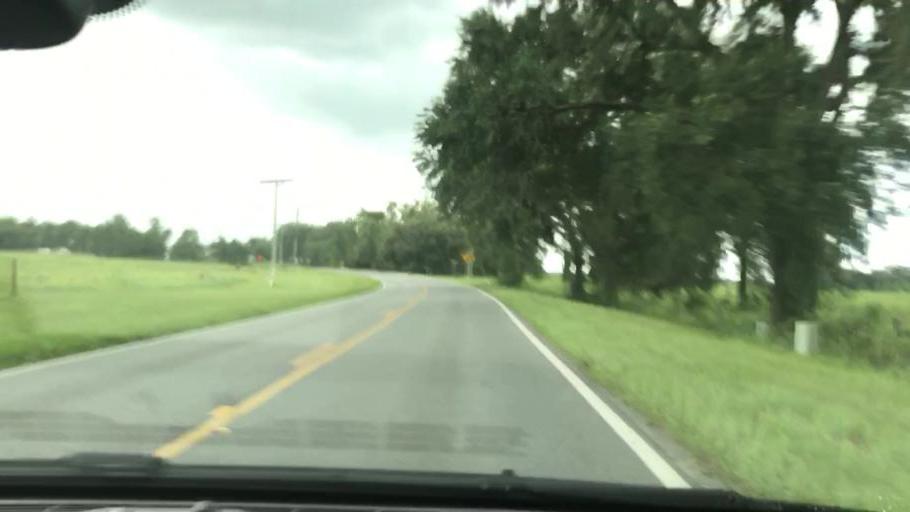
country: US
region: Florida
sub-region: Madison County
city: Madison
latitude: 30.3866
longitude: -83.3004
